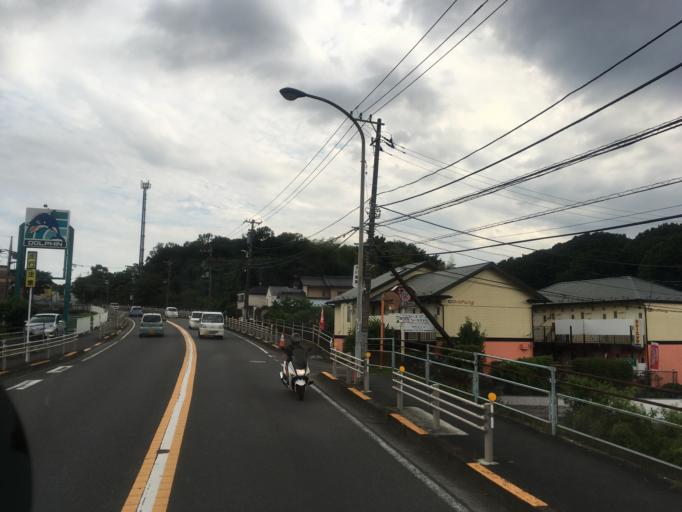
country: JP
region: Tokyo
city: Hachioji
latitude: 35.6349
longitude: 139.3389
